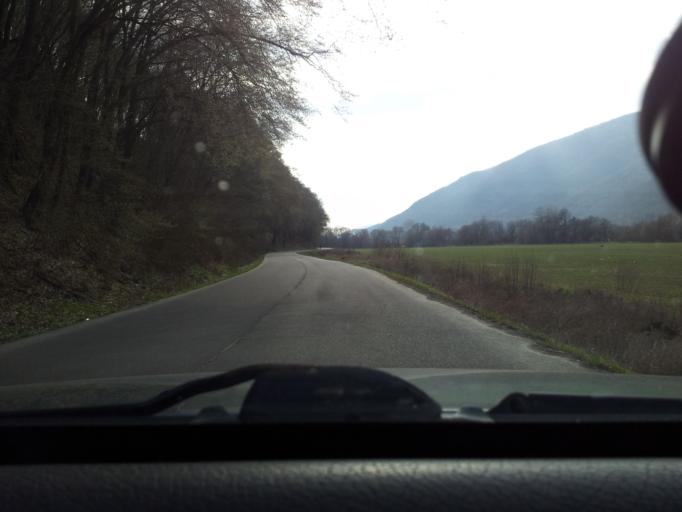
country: SK
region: Banskobystricky
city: Zarnovica
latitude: 48.4378
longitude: 18.6970
